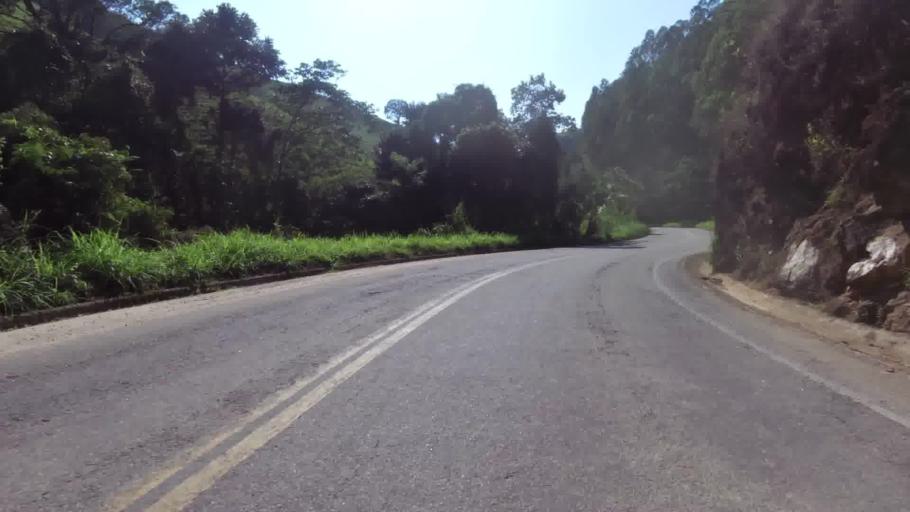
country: BR
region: Espirito Santo
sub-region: Alfredo Chaves
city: Alfredo Chaves
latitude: -20.5924
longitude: -40.7950
